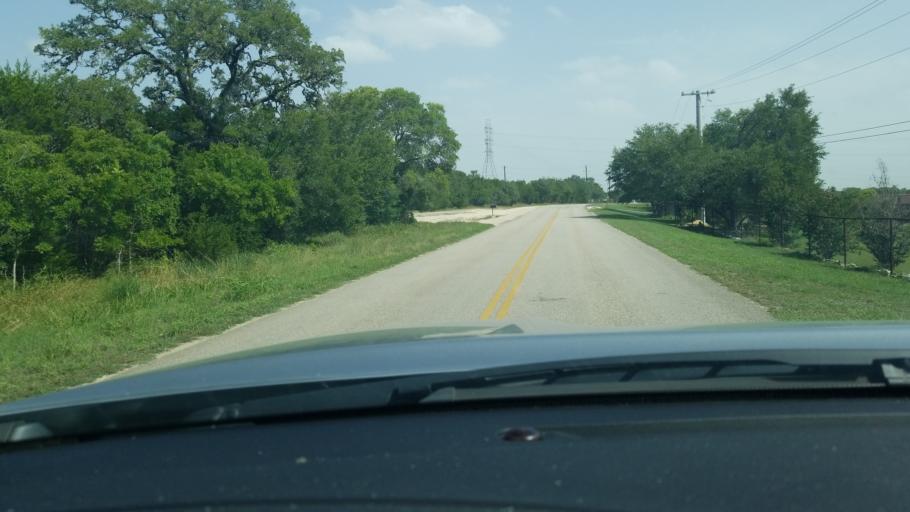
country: US
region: Texas
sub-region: Comal County
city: Bulverde
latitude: 29.7856
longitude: -98.4649
